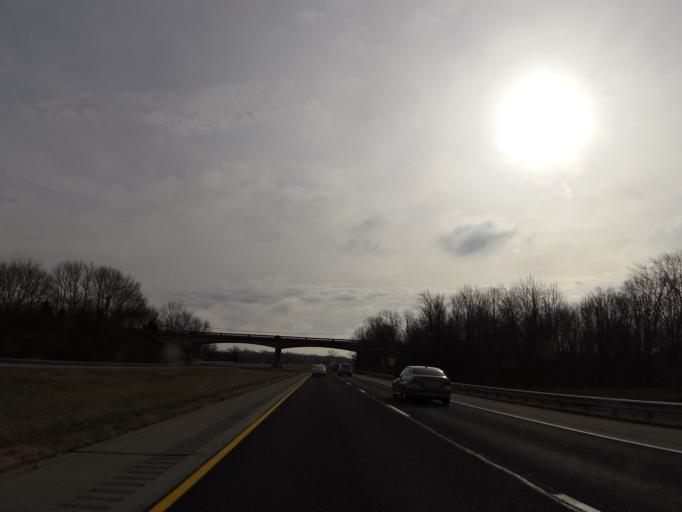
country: US
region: Indiana
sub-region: Marion County
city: Cumberland
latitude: 39.7106
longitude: -86.0030
